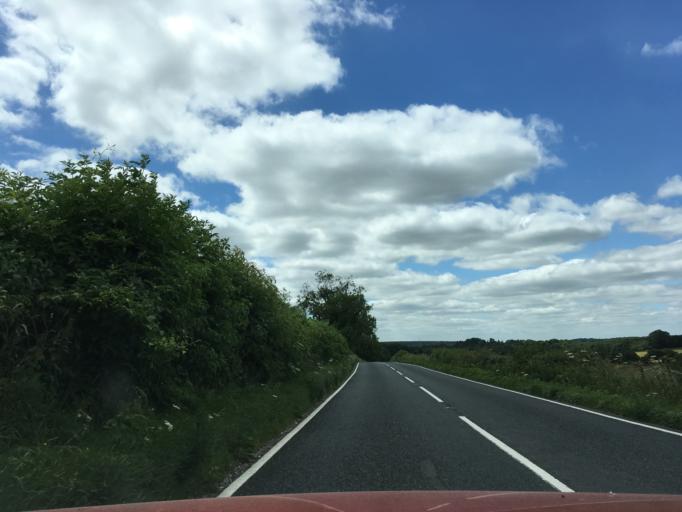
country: GB
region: England
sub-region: Hampshire
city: Highclere
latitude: 51.3013
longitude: -1.4038
